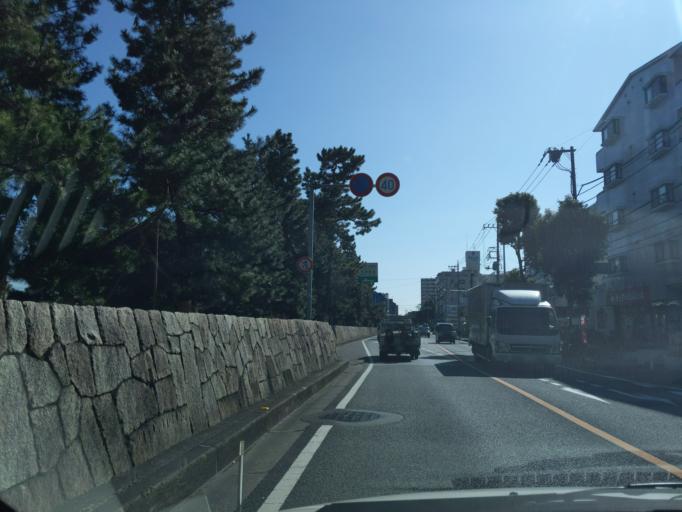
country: JP
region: Saitama
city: Soka
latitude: 35.8390
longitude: 139.8058
